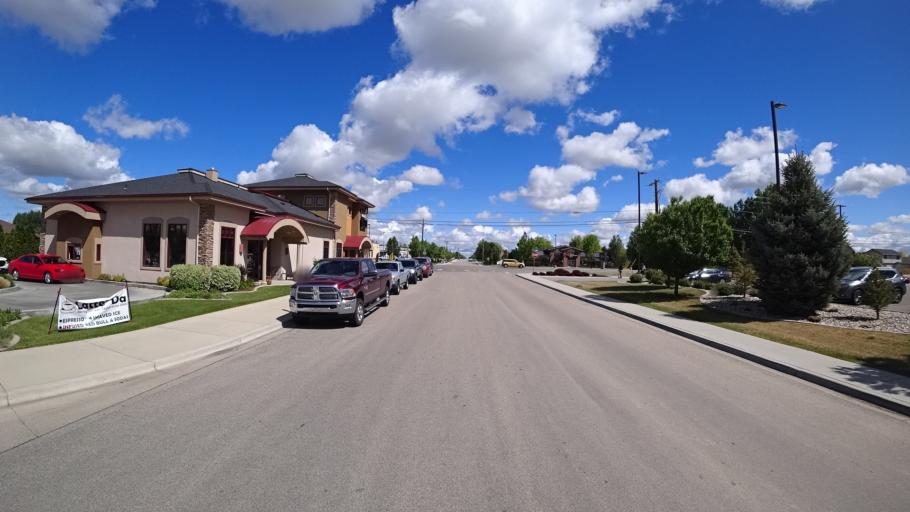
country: US
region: Idaho
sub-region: Ada County
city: Kuna
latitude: 43.4878
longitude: -116.4039
